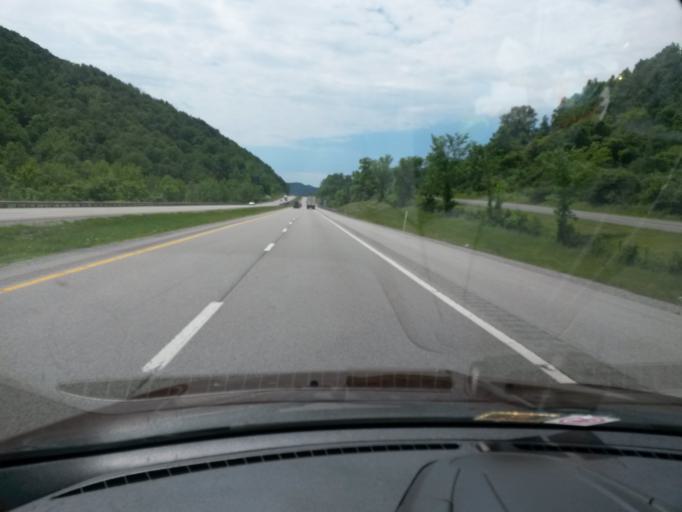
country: US
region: West Virginia
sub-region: Gilmer County
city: Glenville
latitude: 38.8530
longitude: -80.6646
